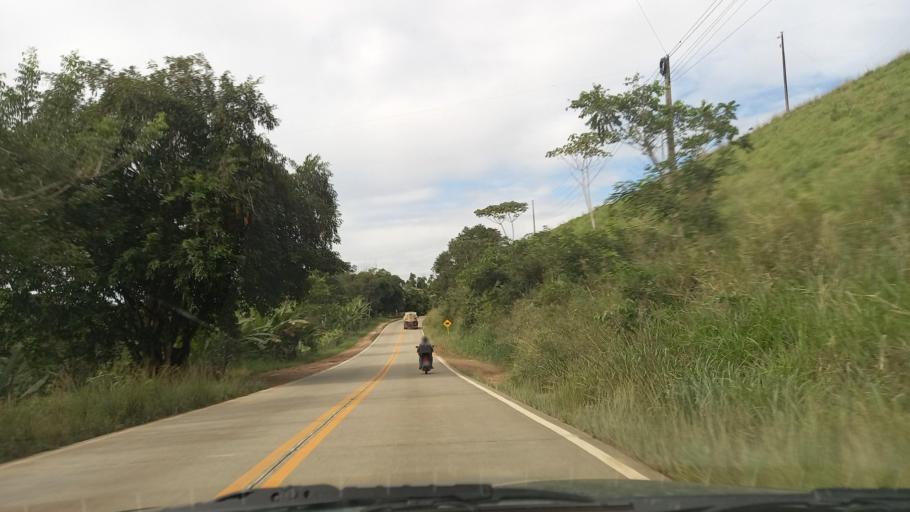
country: BR
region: Pernambuco
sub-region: Maraial
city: Maraial
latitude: -8.7488
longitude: -35.8180
